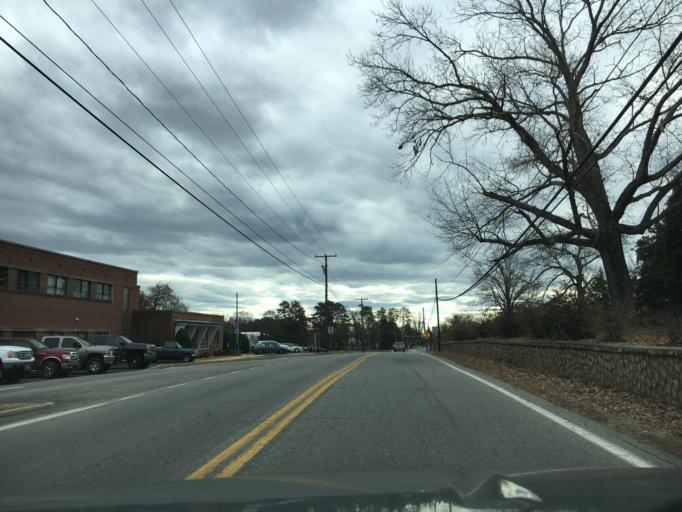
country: US
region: Virginia
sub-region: Halifax County
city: South Boston
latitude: 36.7210
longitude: -78.9039
